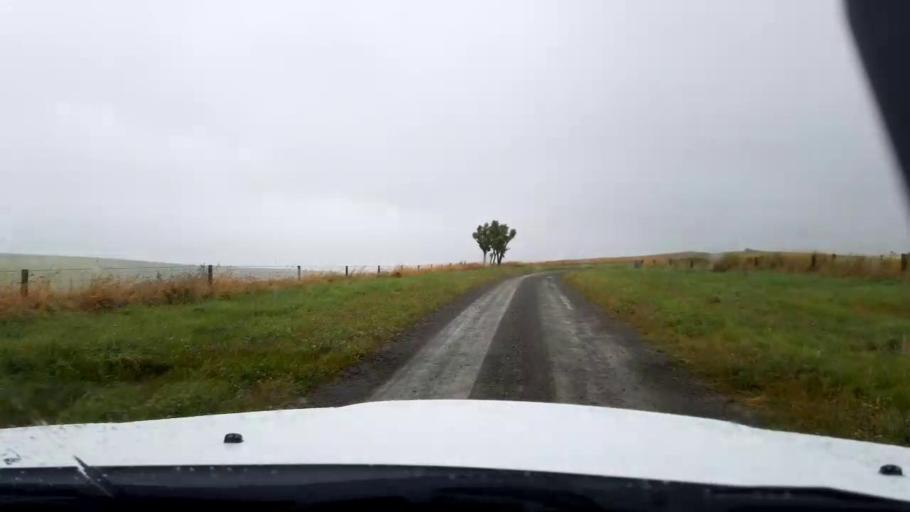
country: NZ
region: Canterbury
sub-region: Timaru District
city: Pleasant Point
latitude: -44.1667
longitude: 171.1709
